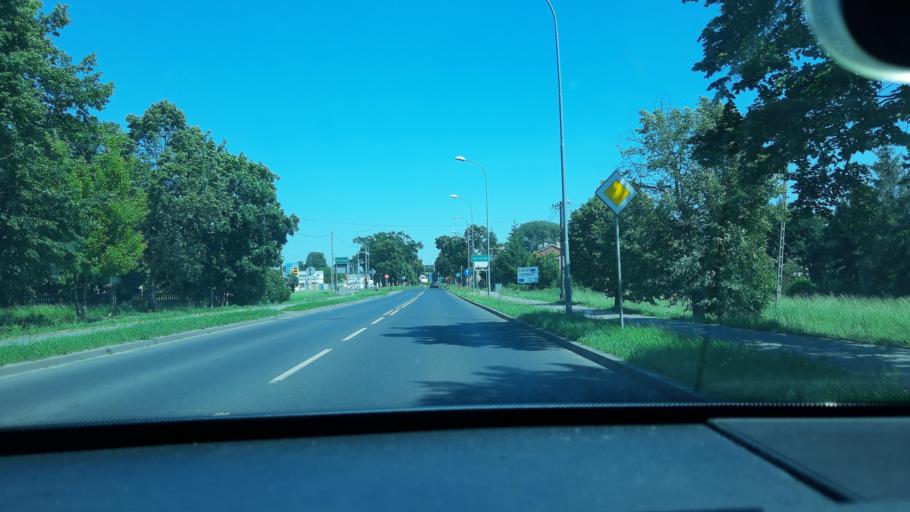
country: PL
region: Lodz Voivodeship
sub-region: Powiat zdunskowolski
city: Zdunska Wola
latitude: 51.6074
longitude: 18.9148
